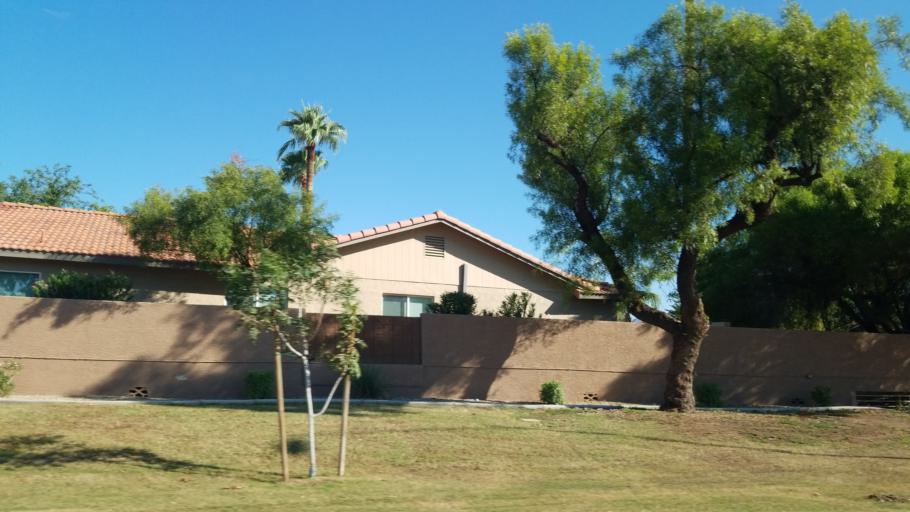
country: US
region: Arizona
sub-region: Maricopa County
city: Scottsdale
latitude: 33.5385
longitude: -111.8979
